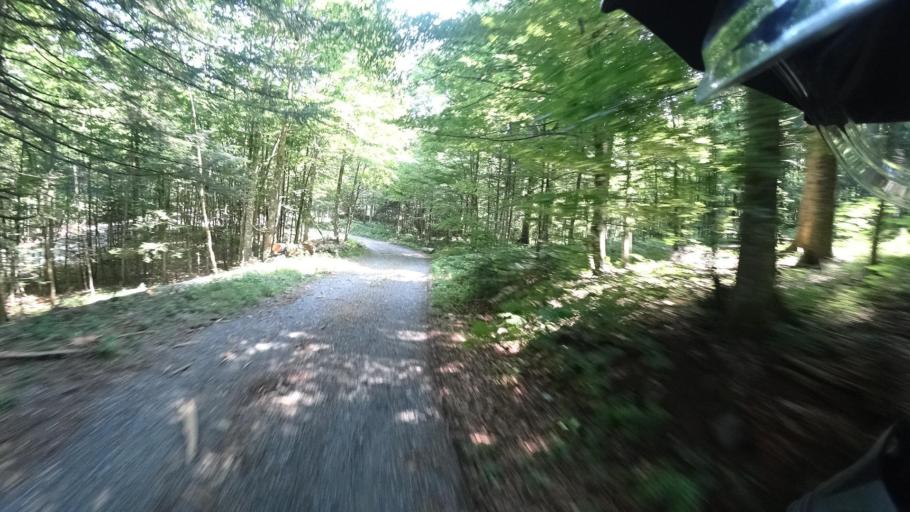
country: HR
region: Primorsko-Goranska
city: Vrbovsko
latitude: 45.3380
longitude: 15.0306
